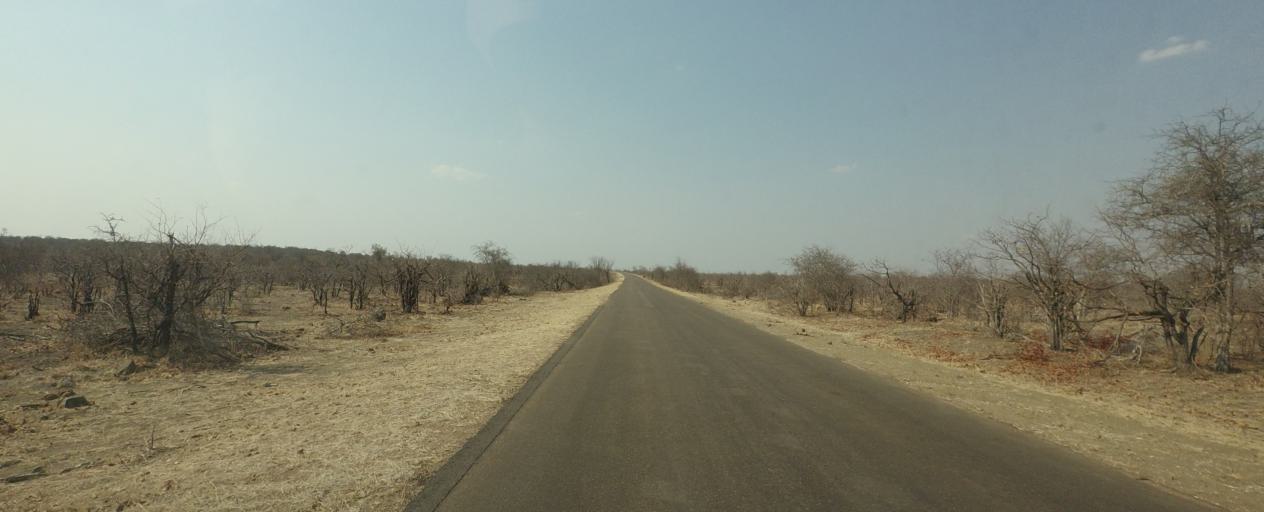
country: ZA
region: Limpopo
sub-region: Mopani District Municipality
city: Giyani
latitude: -23.1251
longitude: 31.3819
